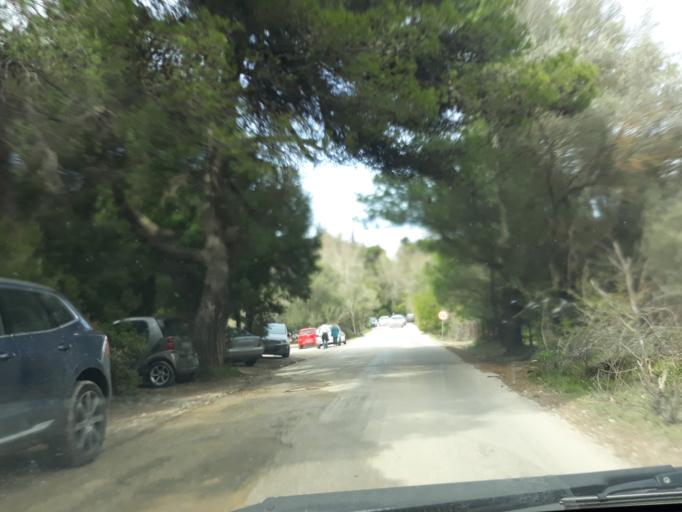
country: GR
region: Attica
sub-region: Nomarchia Anatolikis Attikis
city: Varybobi
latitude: 38.1591
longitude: 23.7919
